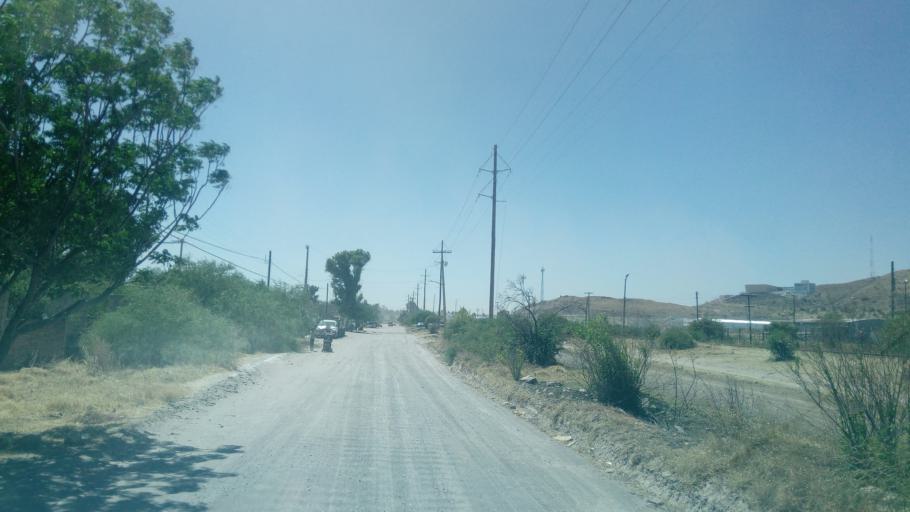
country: MX
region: Durango
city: Victoria de Durango
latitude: 24.0765
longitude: -104.6587
